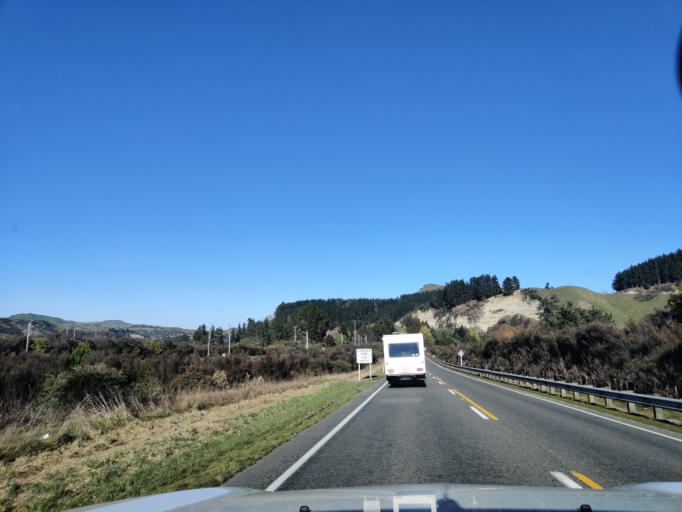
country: NZ
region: Manawatu-Wanganui
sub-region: Ruapehu District
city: Waiouru
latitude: -39.7527
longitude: 175.8329
